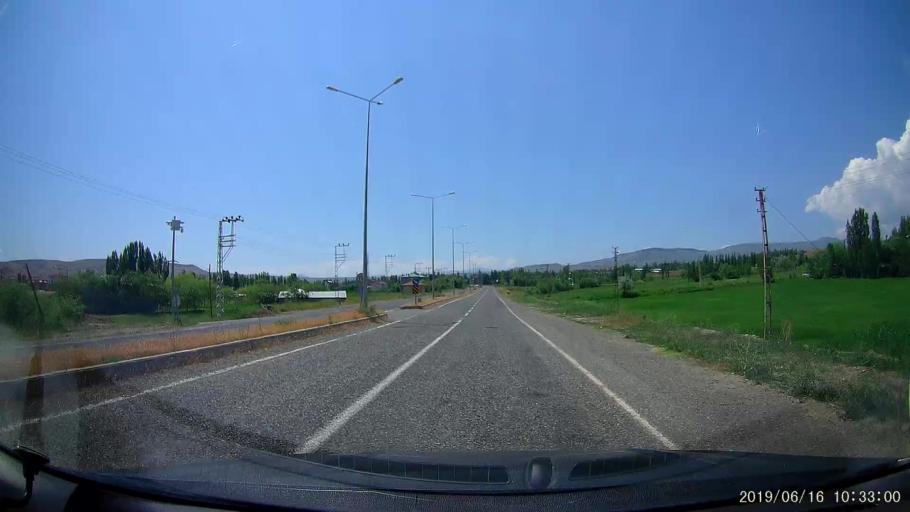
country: TR
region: Igdir
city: Tuzluca
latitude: 40.0451
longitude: 43.6545
